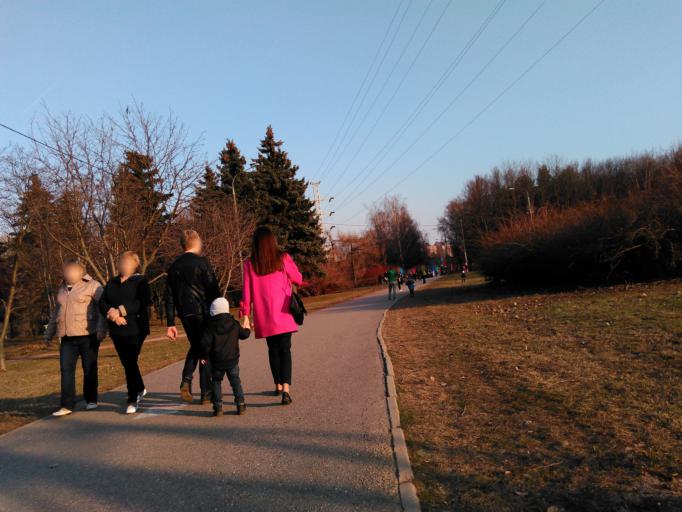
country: RU
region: Moscow
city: Ramenki
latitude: 55.6834
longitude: 37.5014
